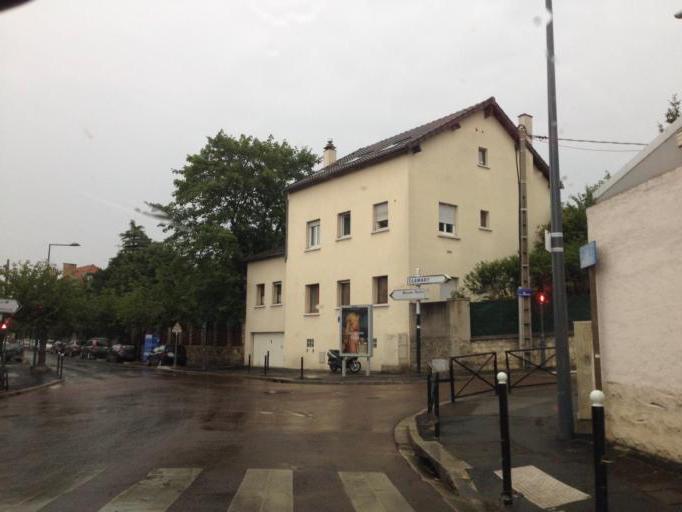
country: FR
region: Ile-de-France
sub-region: Departement des Hauts-de-Seine
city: Meudon
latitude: 48.8103
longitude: 2.2472
